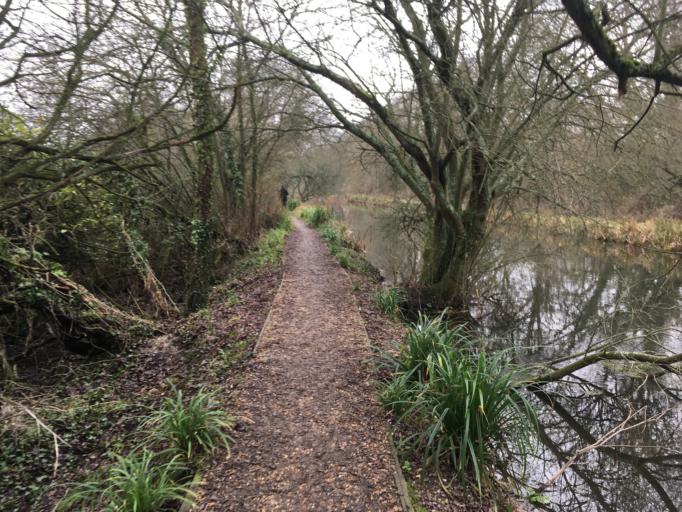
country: GB
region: England
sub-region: Hampshire
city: Compton
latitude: 50.9931
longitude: -1.3408
